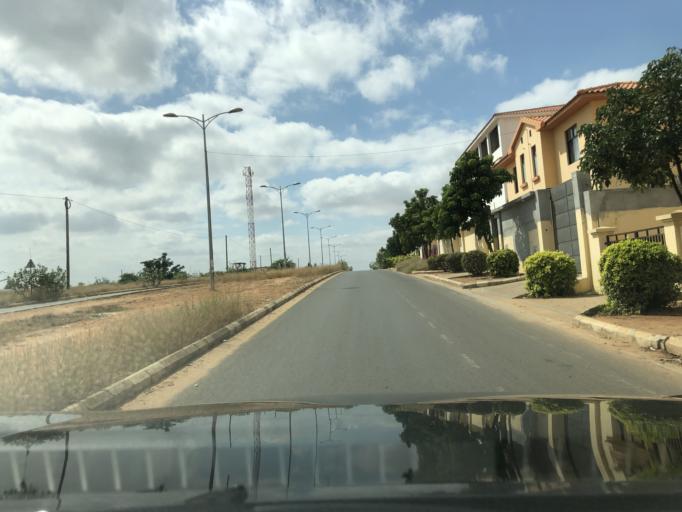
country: AO
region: Luanda
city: Luanda
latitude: -8.9456
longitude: 13.2434
